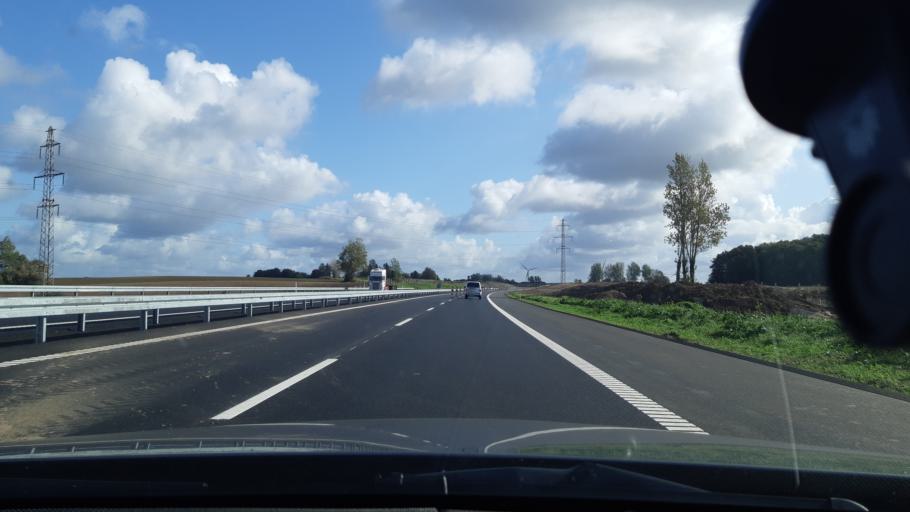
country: DK
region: Zealand
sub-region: Soro Kommune
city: Stenlille
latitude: 55.6613
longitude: 11.6032
